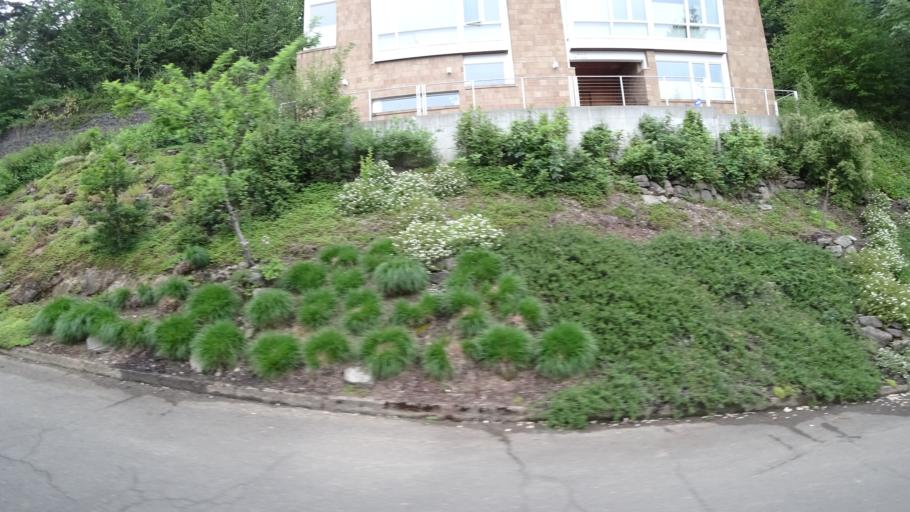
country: US
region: Oregon
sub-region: Multnomah County
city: Portland
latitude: 45.4889
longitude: -122.7000
